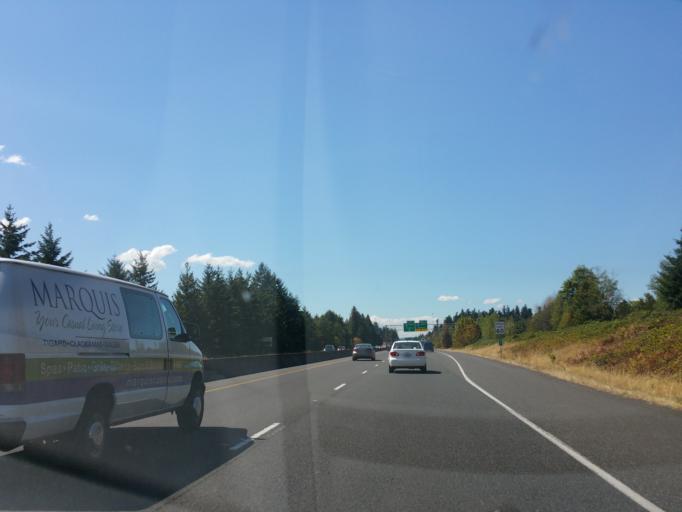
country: US
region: Washington
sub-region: Clark County
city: Mill Plain
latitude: 45.5994
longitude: -122.5332
